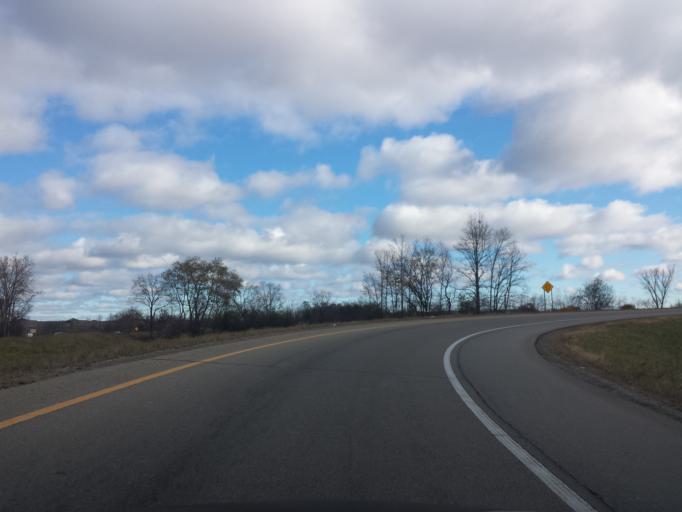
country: US
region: Michigan
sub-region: Oakland County
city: Auburn Hills
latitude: 42.6430
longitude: -83.2401
